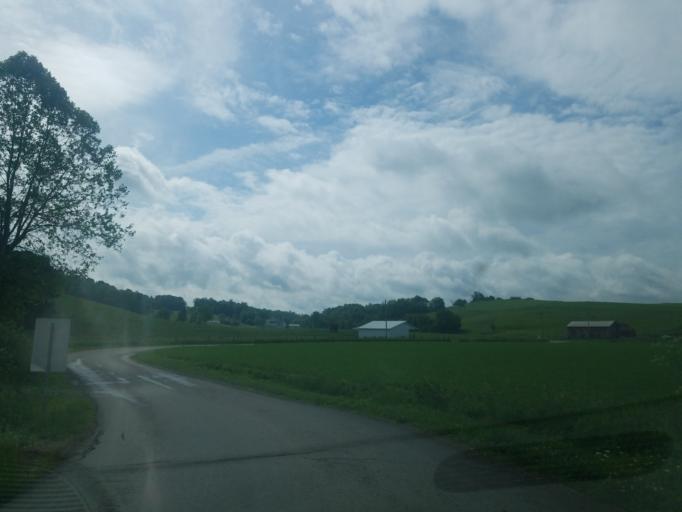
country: US
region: Ohio
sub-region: Holmes County
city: Millersburg
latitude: 40.4711
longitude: -81.8432
